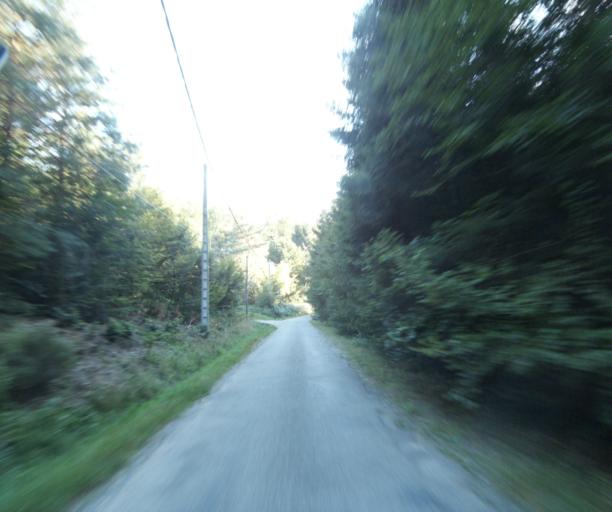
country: FR
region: Lorraine
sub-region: Departement des Vosges
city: Chantraine
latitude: 48.1393
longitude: 6.4259
